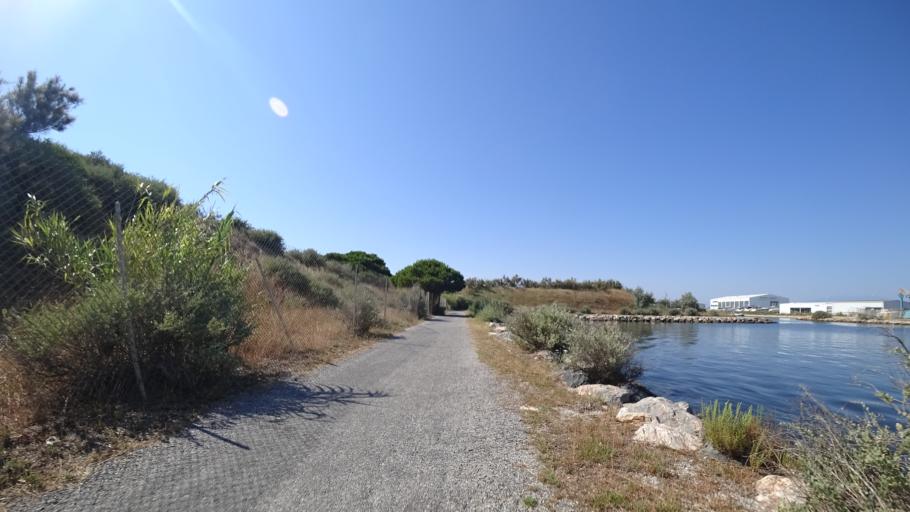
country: FR
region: Languedoc-Roussillon
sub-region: Departement des Pyrenees-Orientales
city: Le Barcares
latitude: 42.8041
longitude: 3.0329
